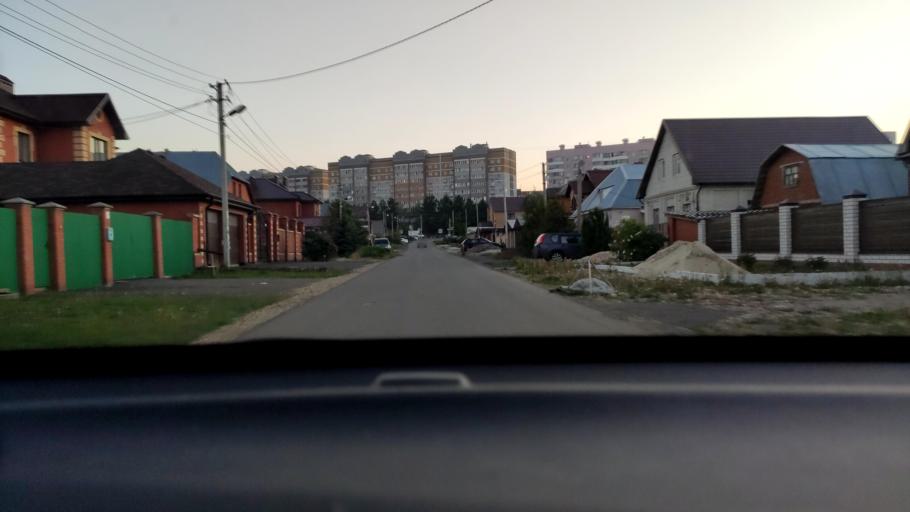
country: RU
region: Tatarstan
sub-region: Gorod Kazan'
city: Kazan
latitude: 55.7839
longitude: 49.2418
